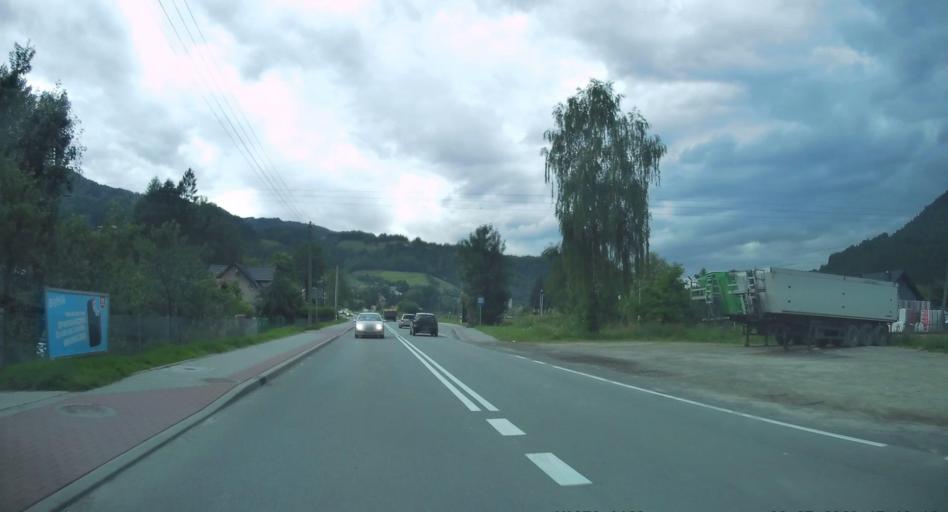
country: PL
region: Lesser Poland Voivodeship
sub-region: Powiat nowosadecki
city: Piwniczna-Zdroj
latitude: 49.4496
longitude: 20.7017
